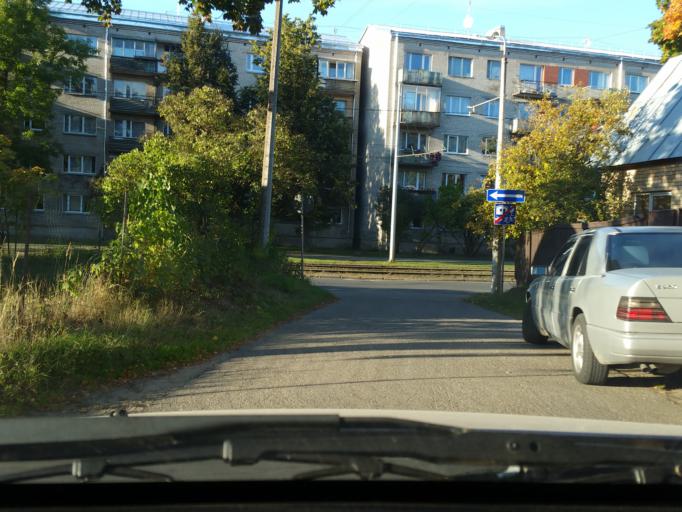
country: LV
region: Riga
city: Jaunciems
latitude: 56.9818
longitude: 24.1868
